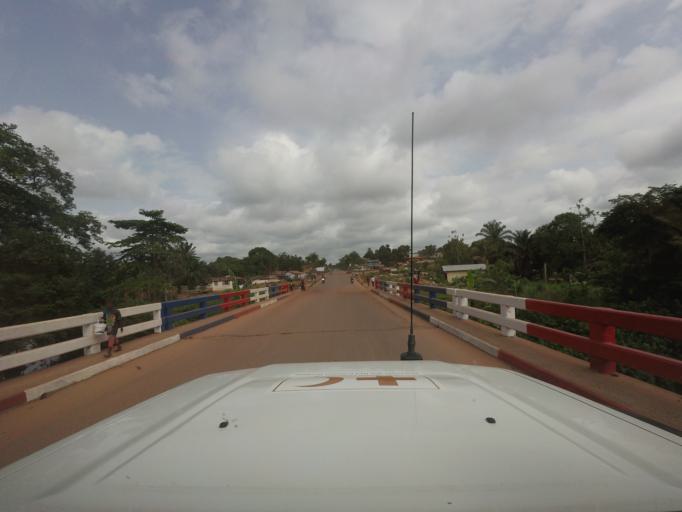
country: LR
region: Bong
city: Gbarnga
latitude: 7.0060
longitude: -9.4788
